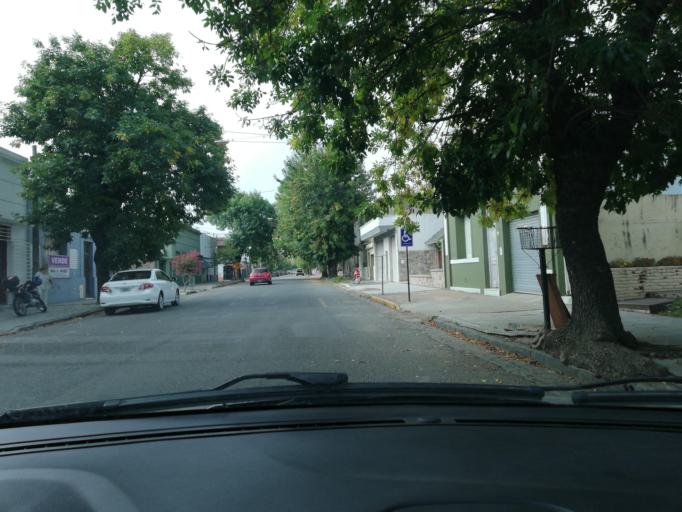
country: AR
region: Buenos Aires
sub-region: Partido de Balcarce
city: Balcarce
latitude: -37.8513
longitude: -58.2515
